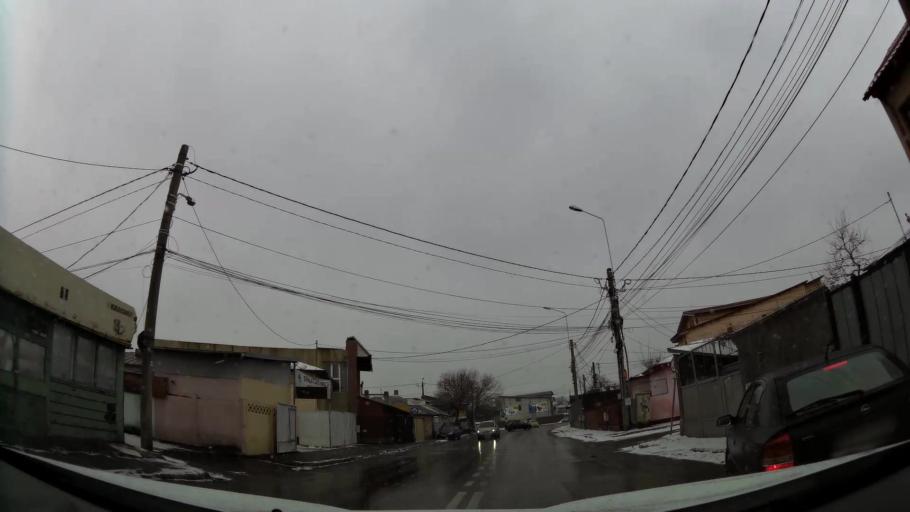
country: RO
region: Prahova
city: Ploiesti
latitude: 44.9534
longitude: 26.0172
